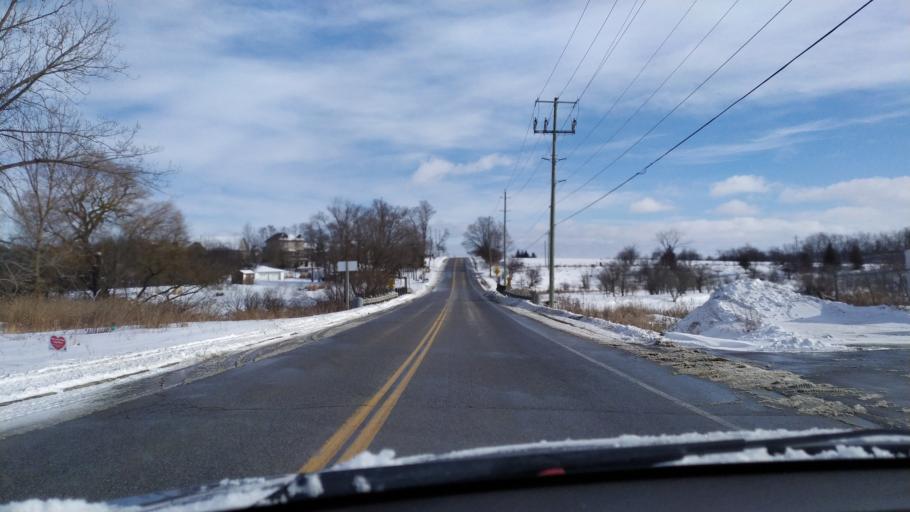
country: CA
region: Ontario
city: Stratford
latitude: 43.4701
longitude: -80.7644
